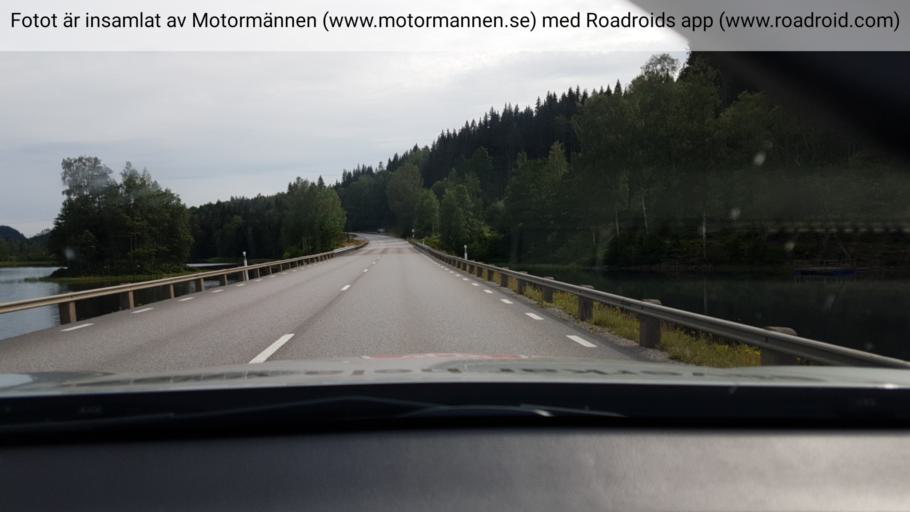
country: SE
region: Vaestra Goetaland
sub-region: Bengtsfors Kommun
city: Dals Langed
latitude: 59.0528
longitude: 12.4369
